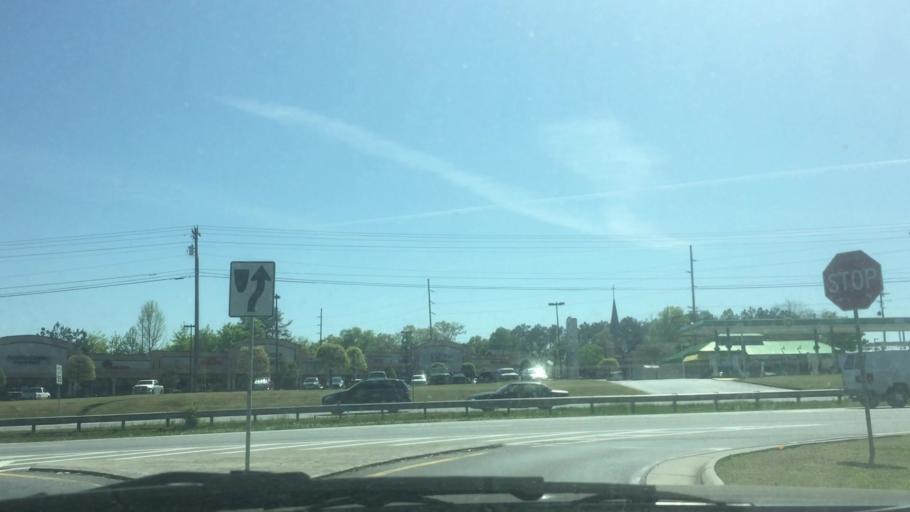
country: US
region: Georgia
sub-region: Cobb County
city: Acworth
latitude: 34.0389
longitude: -84.6905
